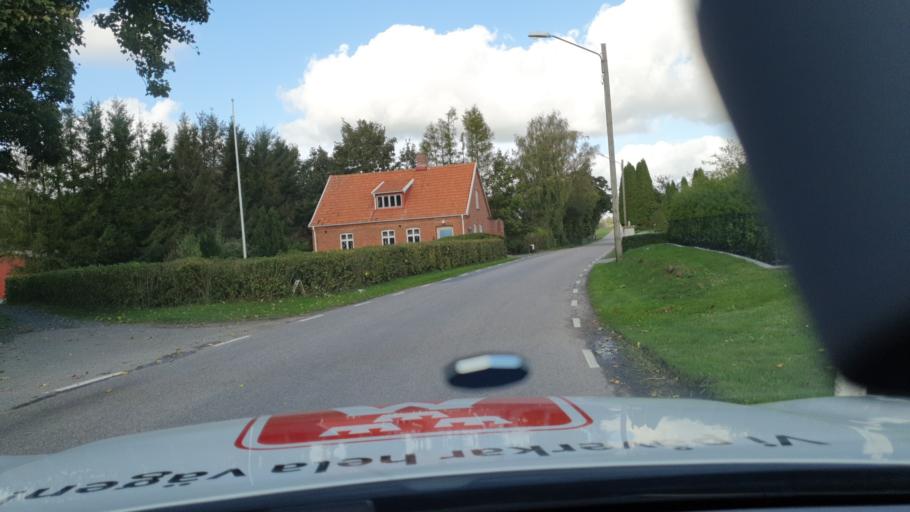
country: SE
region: Skane
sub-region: Ystads Kommun
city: Kopingebro
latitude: 55.4835
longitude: 13.9504
